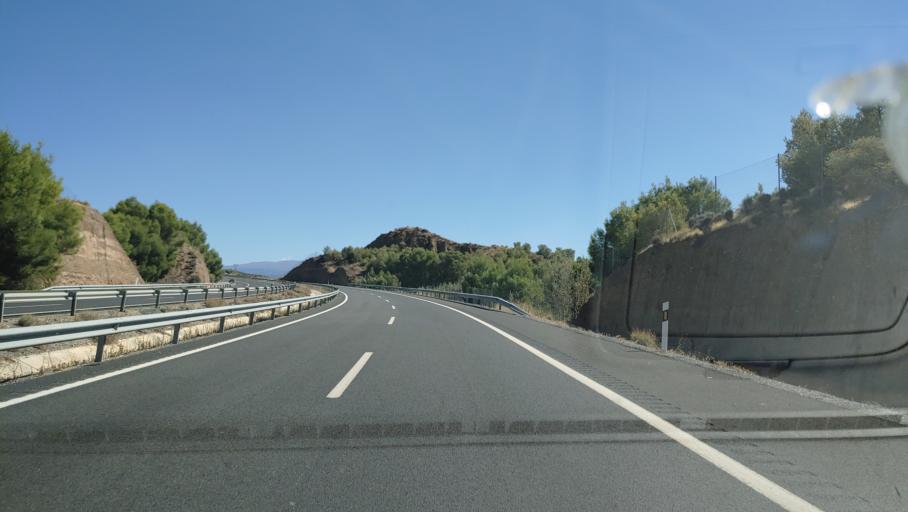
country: ES
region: Andalusia
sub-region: Provincia de Granada
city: Guadix
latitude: 37.2917
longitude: -3.1121
